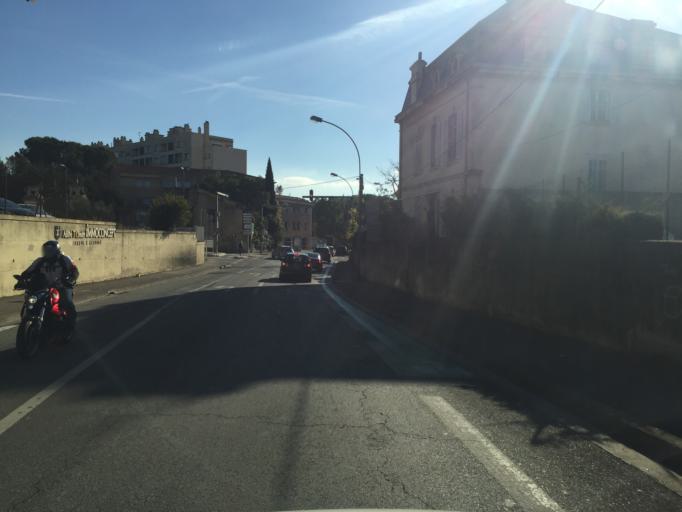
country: FR
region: Provence-Alpes-Cote d'Azur
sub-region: Departement des Bouches-du-Rhone
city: Salon-de-Provence
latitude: 43.6420
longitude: 5.1028
